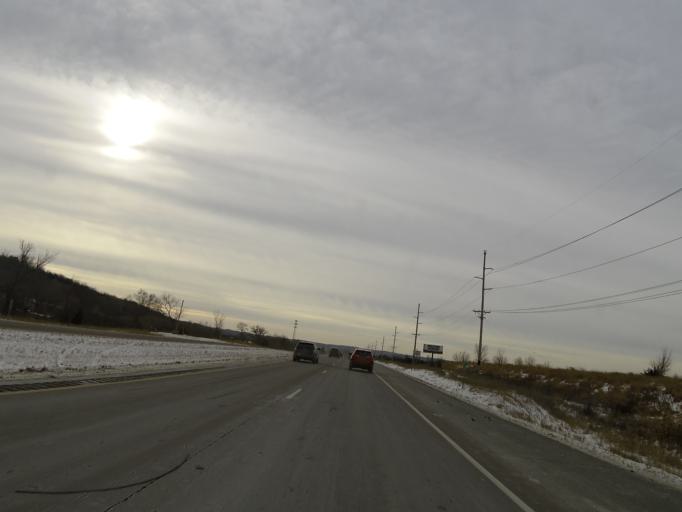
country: US
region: Minnesota
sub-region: Carver County
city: Carver
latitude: 44.7465
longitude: -93.5871
